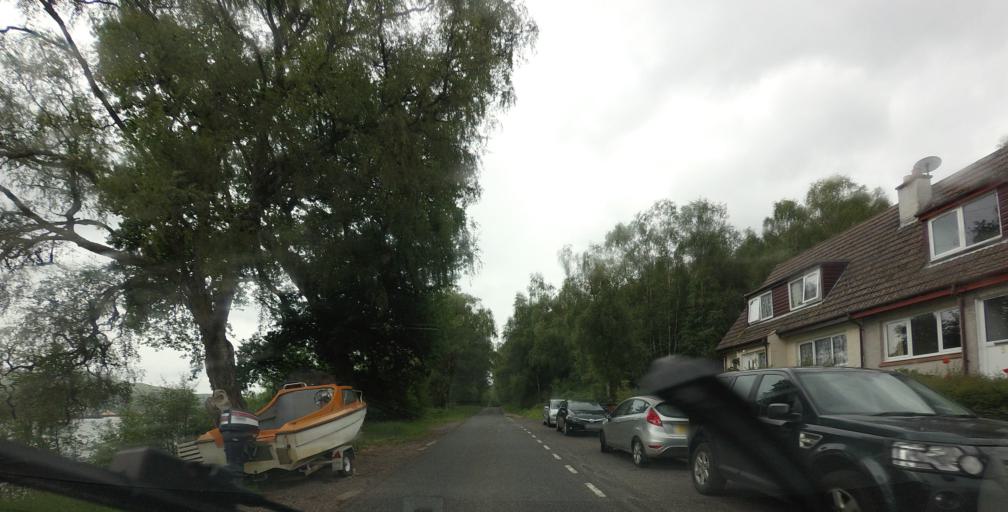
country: GB
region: Scotland
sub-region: Highland
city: Fort William
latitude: 56.8361
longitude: -5.1470
